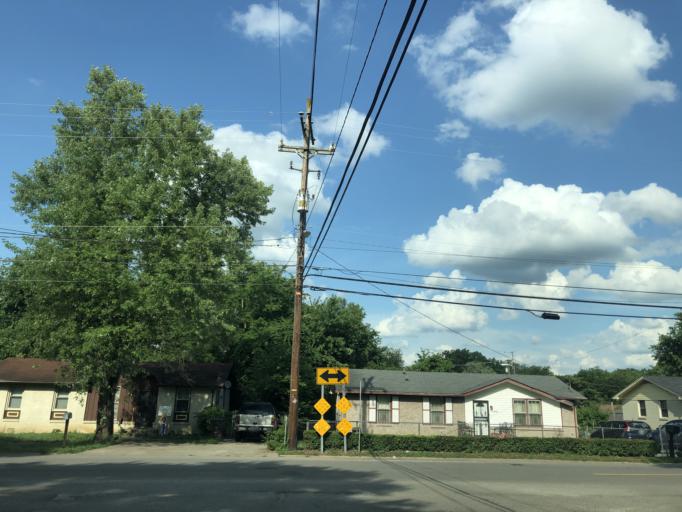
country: US
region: Tennessee
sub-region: Davidson County
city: Nashville
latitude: 36.2251
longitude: -86.8268
